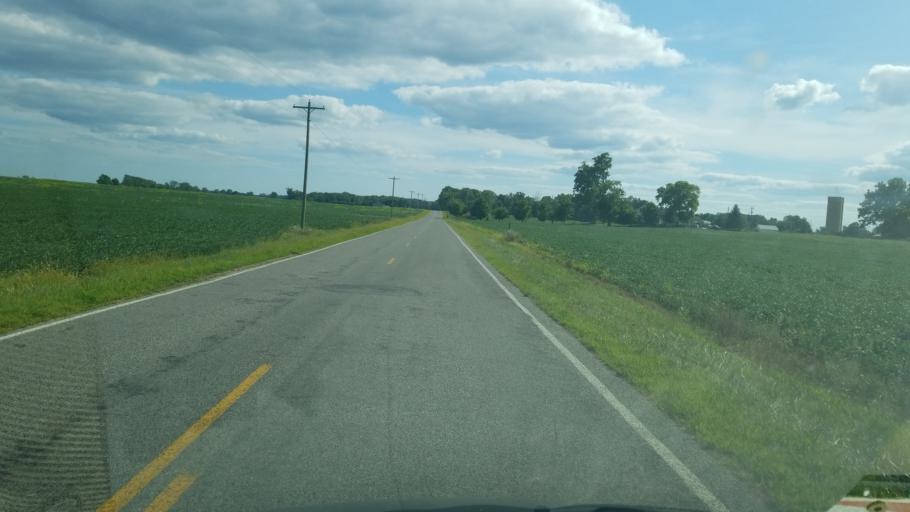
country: US
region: Ohio
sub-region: Logan County
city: De Graff
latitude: 40.2535
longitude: -83.9281
